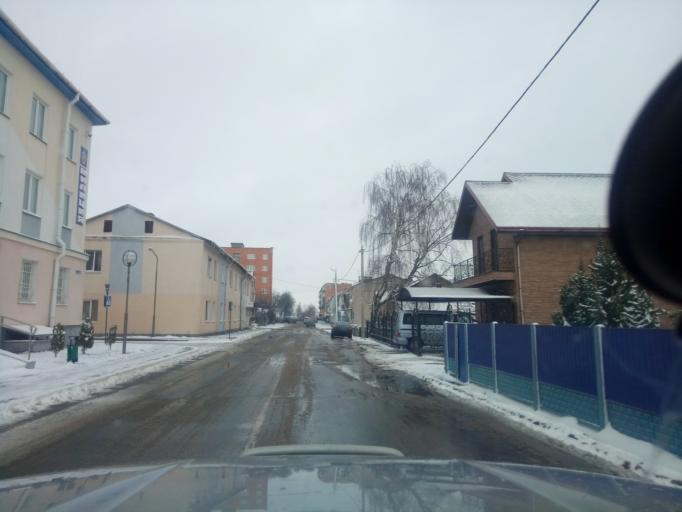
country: BY
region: Minsk
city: Kapyl'
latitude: 53.1524
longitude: 27.0862
